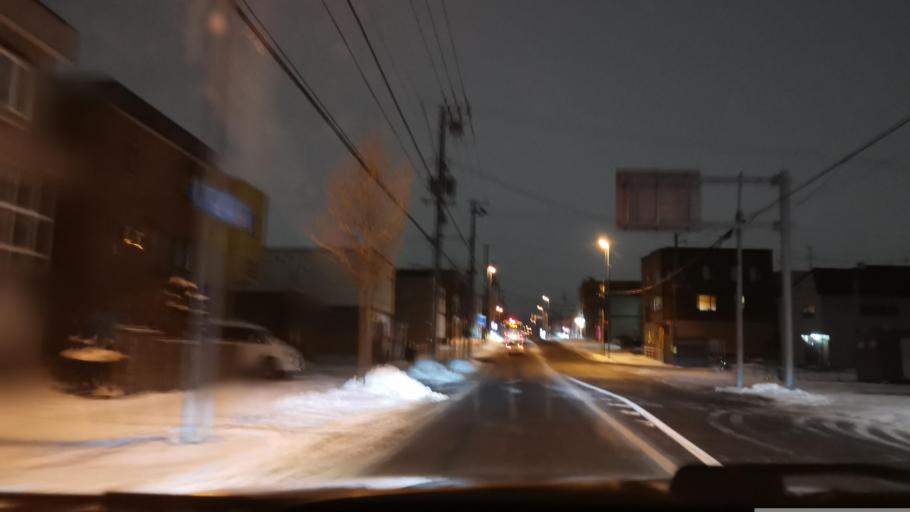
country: JP
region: Hokkaido
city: Sapporo
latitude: 43.0622
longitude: 141.4168
